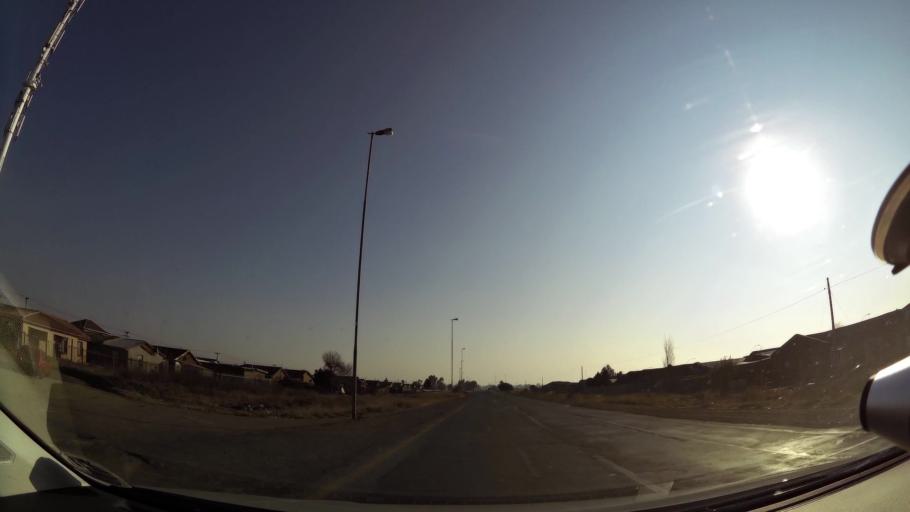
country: ZA
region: Orange Free State
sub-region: Mangaung Metropolitan Municipality
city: Bloemfontein
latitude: -29.1509
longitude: 26.2653
